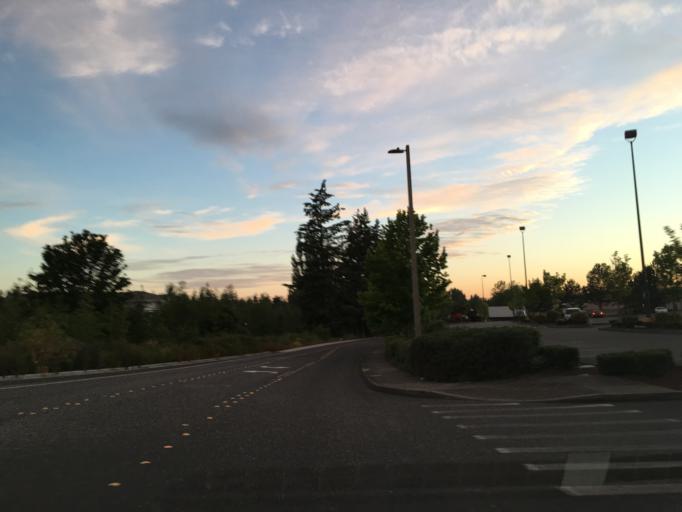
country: US
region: Washington
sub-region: Whatcom County
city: Bellingham
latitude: 48.7847
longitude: -122.4792
